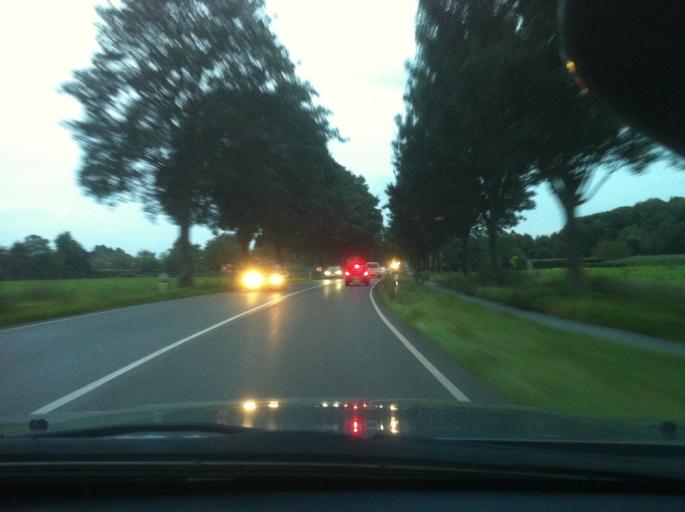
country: DE
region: North Rhine-Westphalia
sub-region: Regierungsbezirk Dusseldorf
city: Kleve
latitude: 51.7525
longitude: 6.1577
